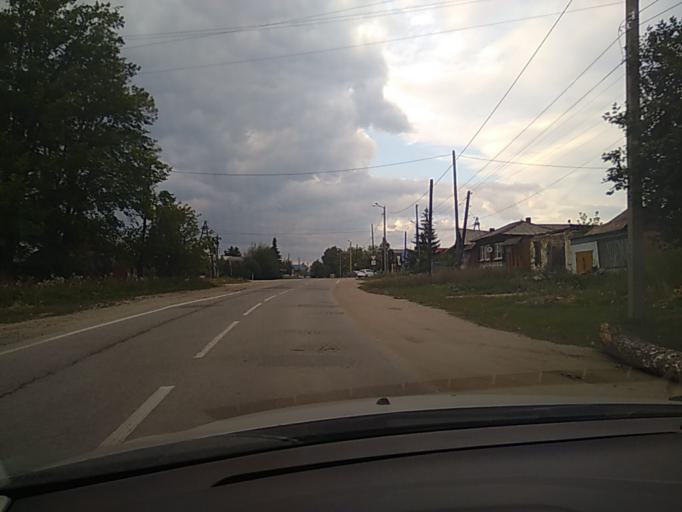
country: RU
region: Chelyabinsk
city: Kyshtym
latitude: 55.6946
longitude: 60.5519
